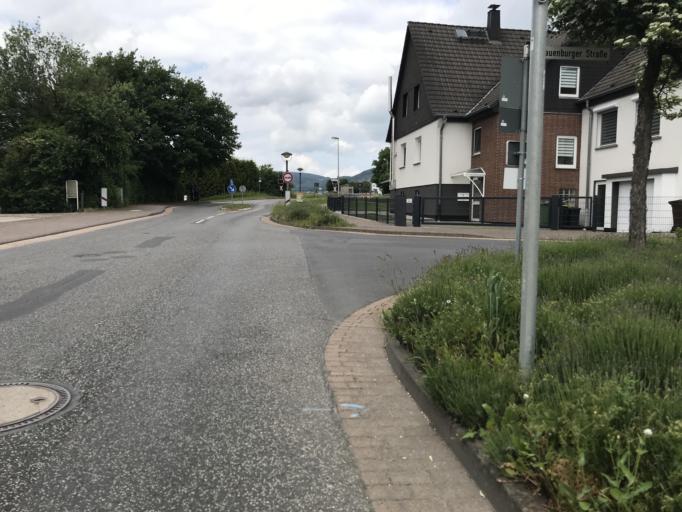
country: DE
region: Hesse
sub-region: Regierungsbezirk Kassel
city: Baunatal
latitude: 51.2536
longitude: 9.3828
